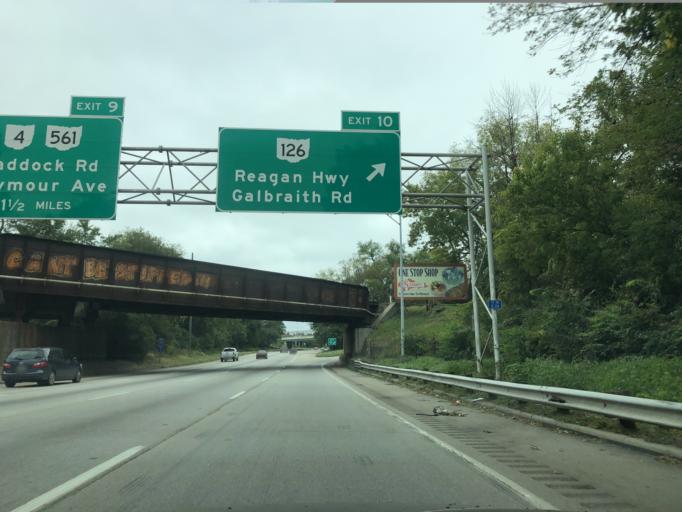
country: US
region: Ohio
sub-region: Hamilton County
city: Lockland
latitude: 39.2147
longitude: -84.4610
